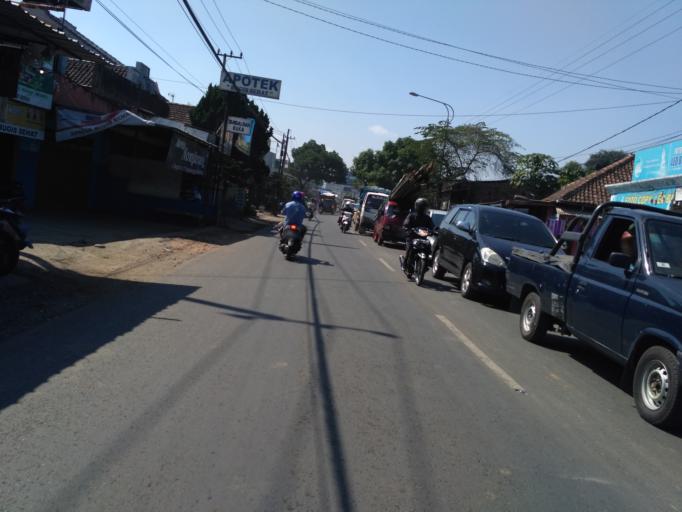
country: ID
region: East Java
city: Malang
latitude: -7.9525
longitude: 112.6875
